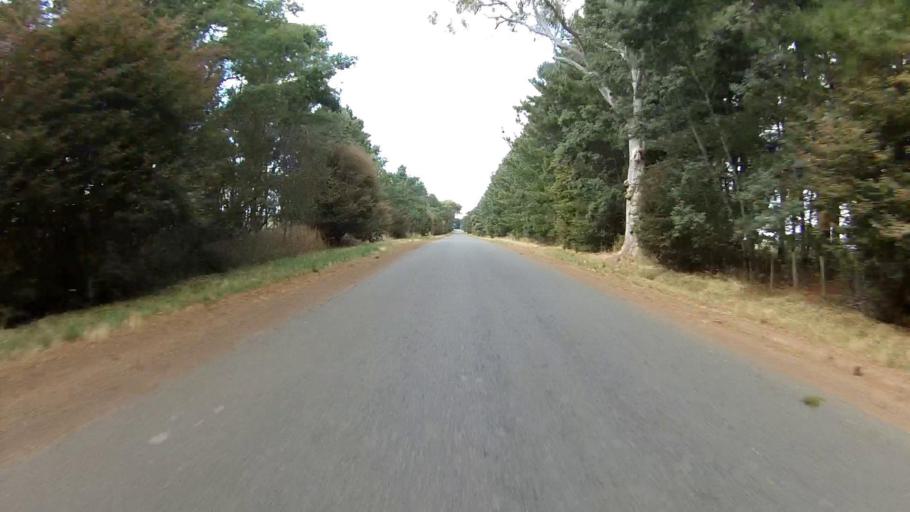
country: AU
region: Tasmania
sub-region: Northern Midlands
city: Evandale
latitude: -41.6869
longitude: 147.3601
